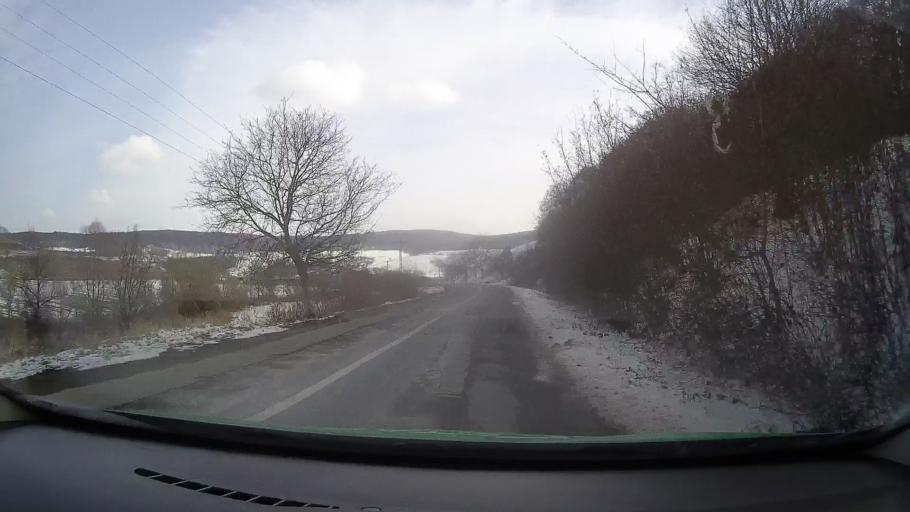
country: RO
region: Mures
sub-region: Comuna Apold
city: Apold
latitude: 46.1418
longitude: 24.8157
